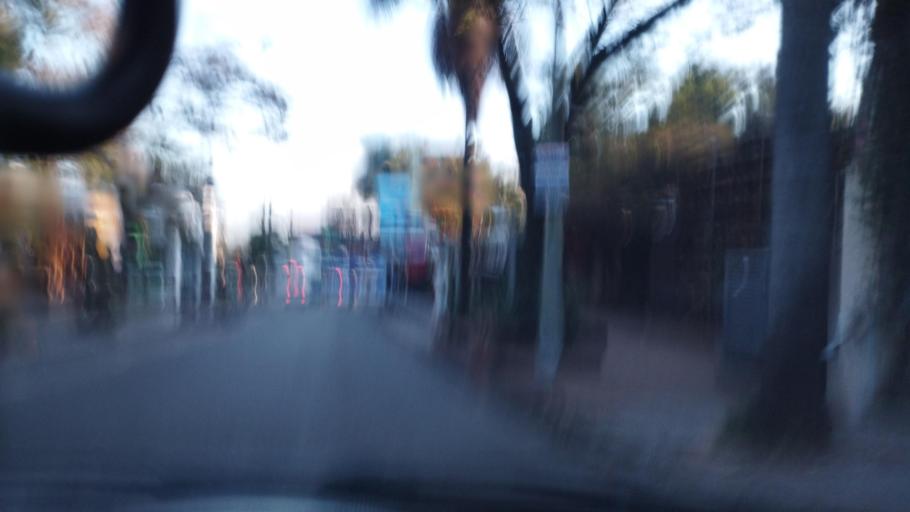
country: PY
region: Asuncion
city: Asuncion
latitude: -25.2863
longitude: -57.5767
